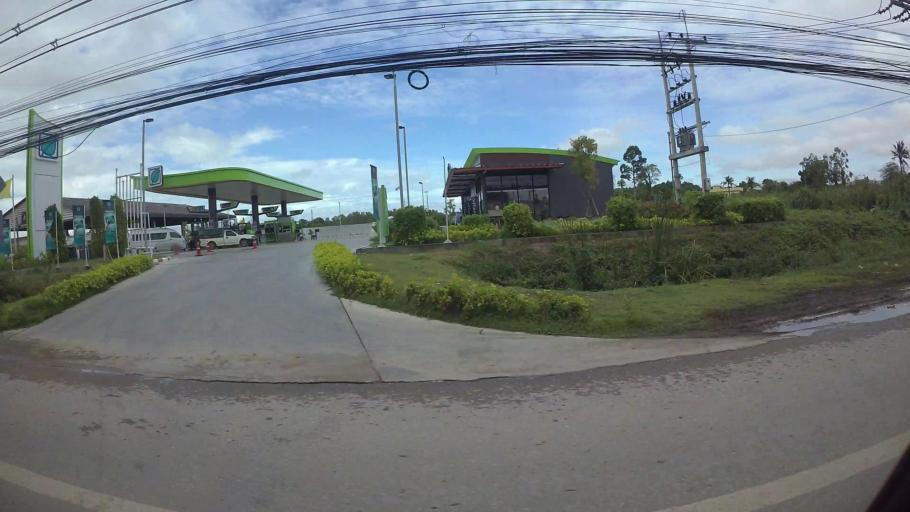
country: TH
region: Rayong
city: Rayong
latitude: 12.7002
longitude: 101.1904
